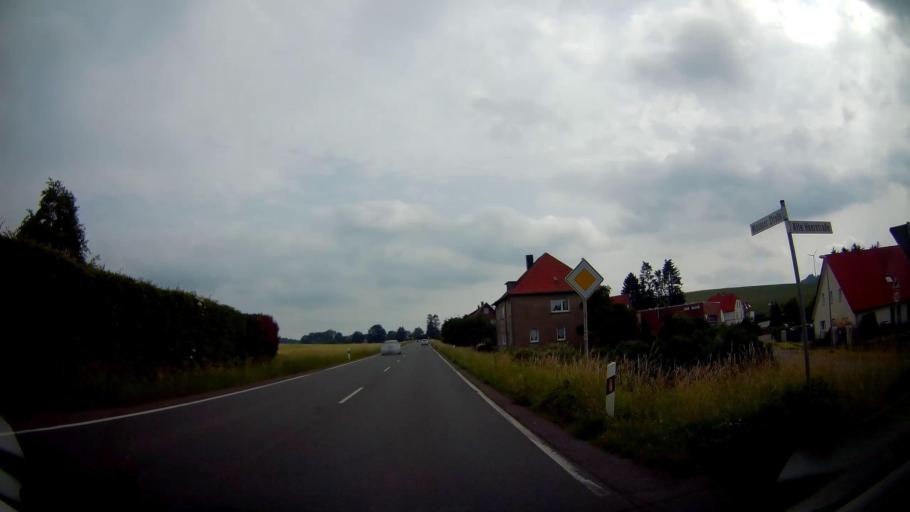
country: DE
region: North Rhine-Westphalia
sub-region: Regierungsbezirk Detmold
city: Herford
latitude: 52.1430
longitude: 8.6999
